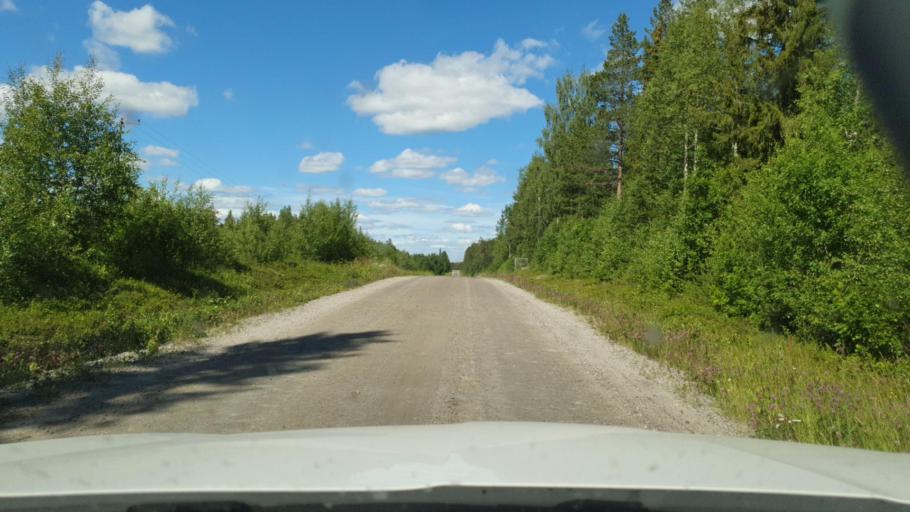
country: SE
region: Vaesterbotten
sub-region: Skelleftea Kommun
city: Byske
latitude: 65.1411
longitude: 21.1792
